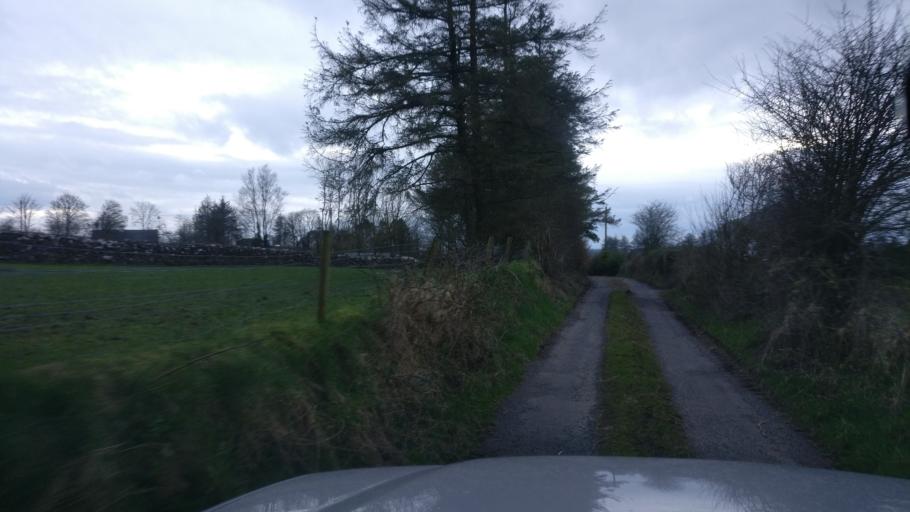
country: IE
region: Connaught
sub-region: County Galway
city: Loughrea
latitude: 53.2687
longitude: -8.4700
